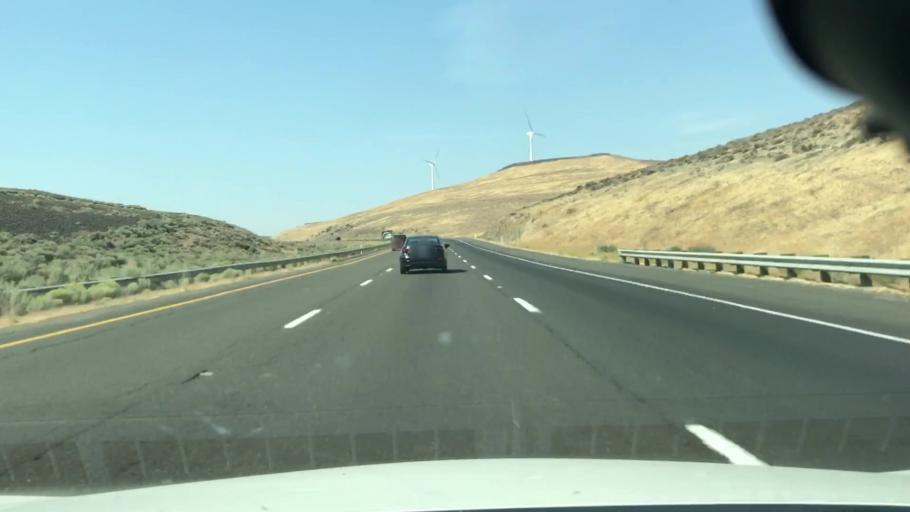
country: US
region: Washington
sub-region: Kittitas County
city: Kittitas
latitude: 46.9450
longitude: -120.1582
